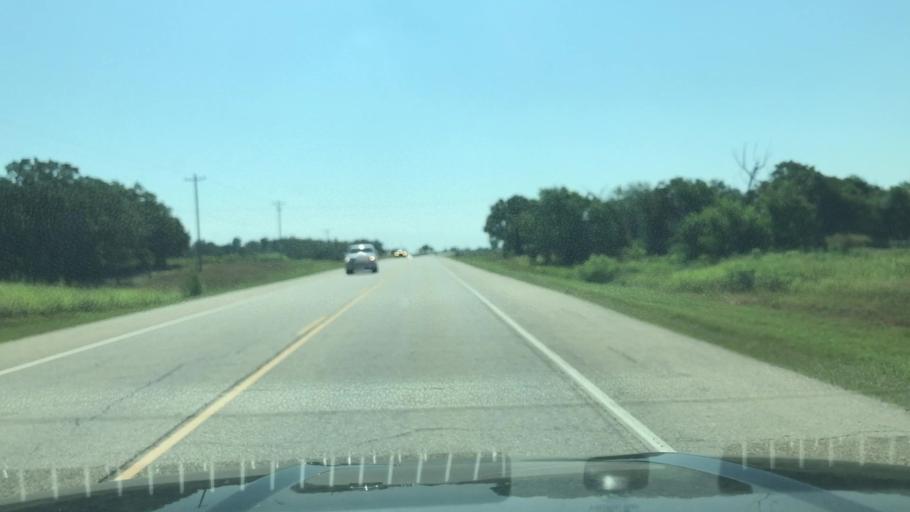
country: US
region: Oklahoma
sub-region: Creek County
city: Mannford
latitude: 36.0010
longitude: -96.3711
